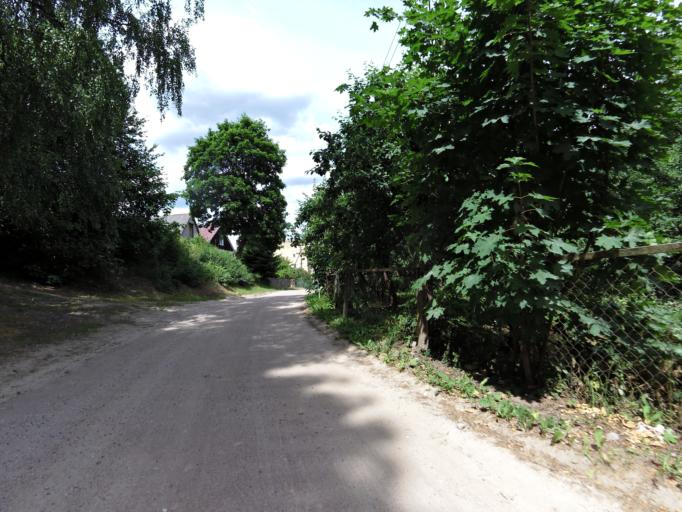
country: LT
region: Vilnius County
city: Rasos
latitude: 54.6724
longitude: 25.3182
